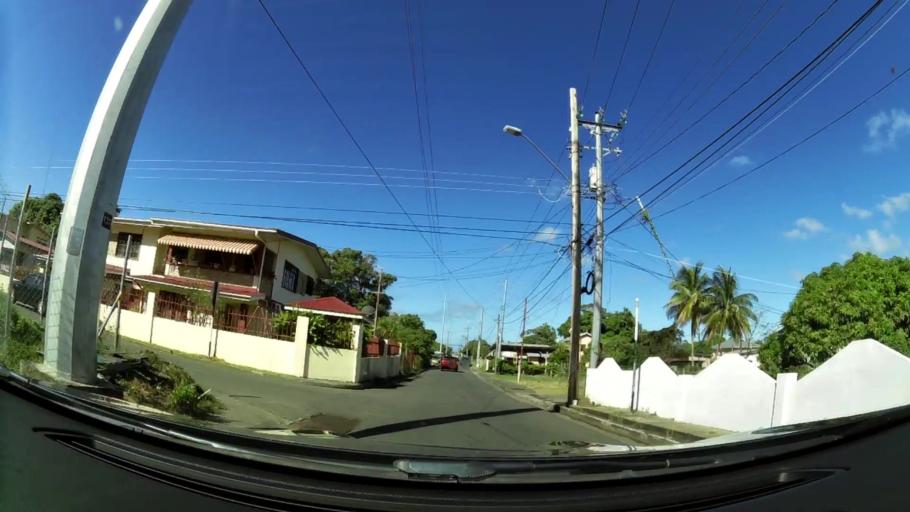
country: TT
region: Tobago
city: Scarborough
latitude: 11.1592
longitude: -60.8088
